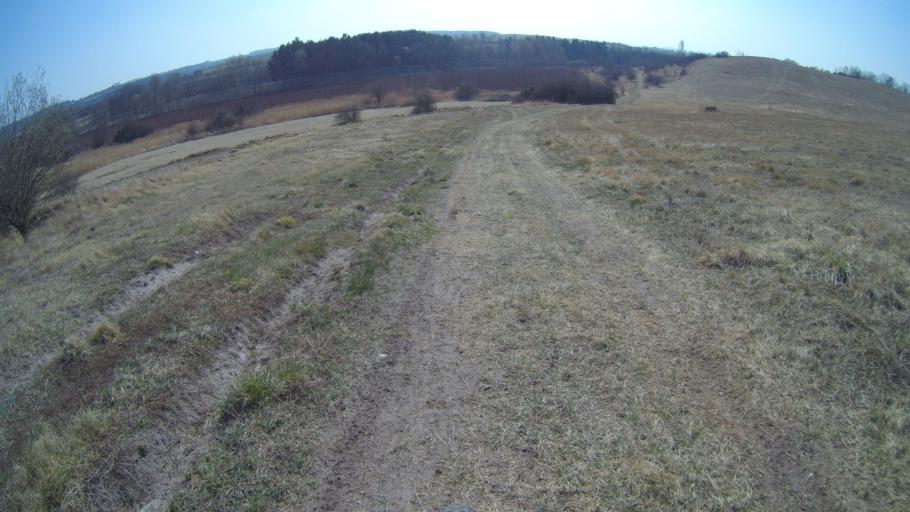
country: CZ
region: Ustecky
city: Mecholupy
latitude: 50.2570
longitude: 13.5478
